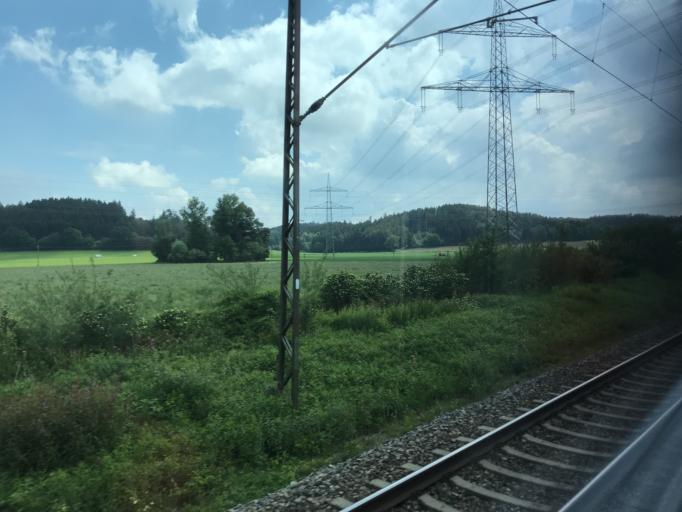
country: DE
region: Bavaria
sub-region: Swabia
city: Offingen
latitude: 48.4750
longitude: 10.3852
